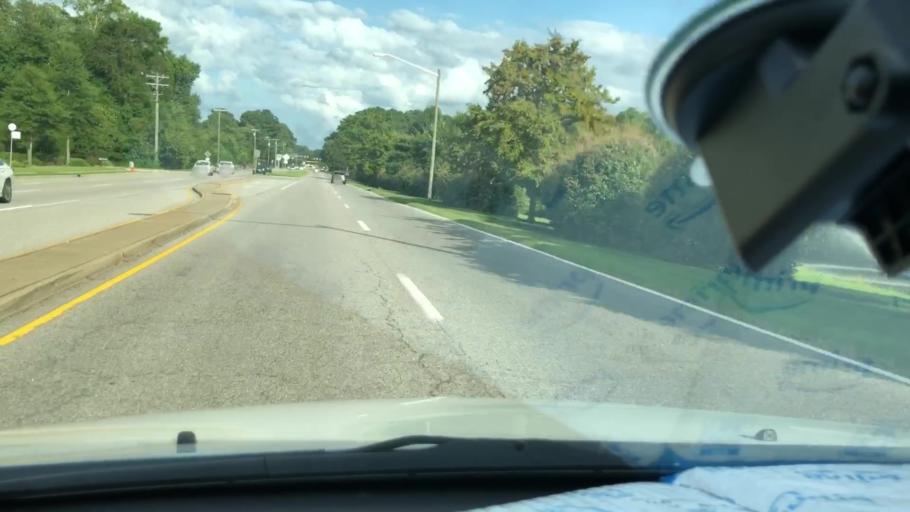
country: US
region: Virginia
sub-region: City of Chesapeake
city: Chesapeake
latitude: 36.7117
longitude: -76.2764
